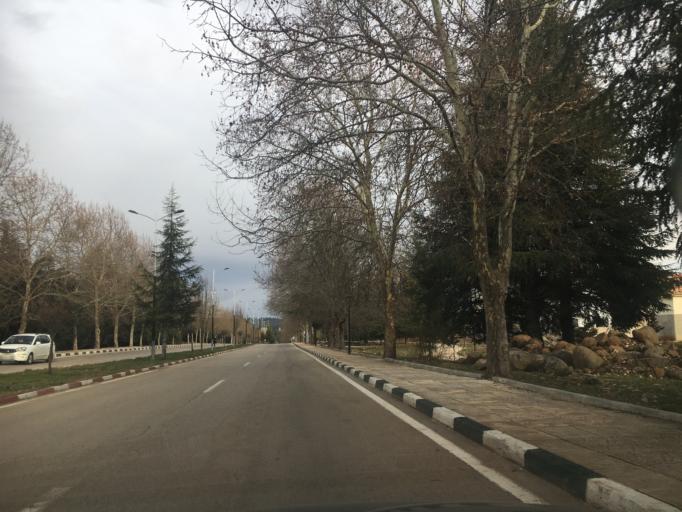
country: MA
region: Meknes-Tafilalet
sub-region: Ifrane
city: Ifrane
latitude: 33.5281
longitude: -5.1273
